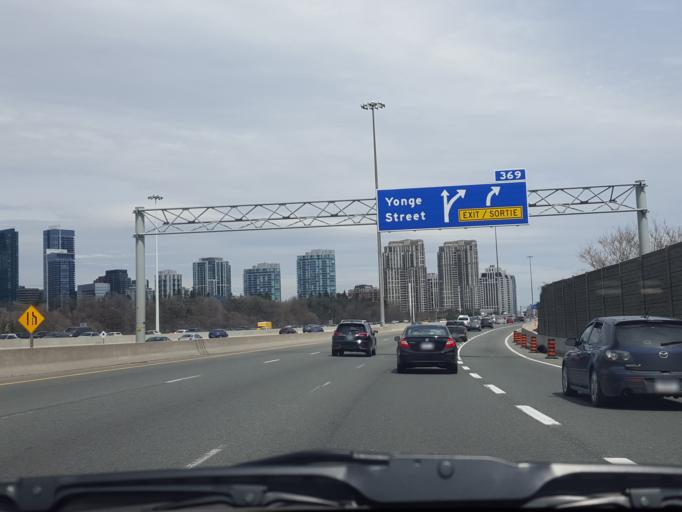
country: CA
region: Ontario
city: North York
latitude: 43.7485
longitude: -79.4150
